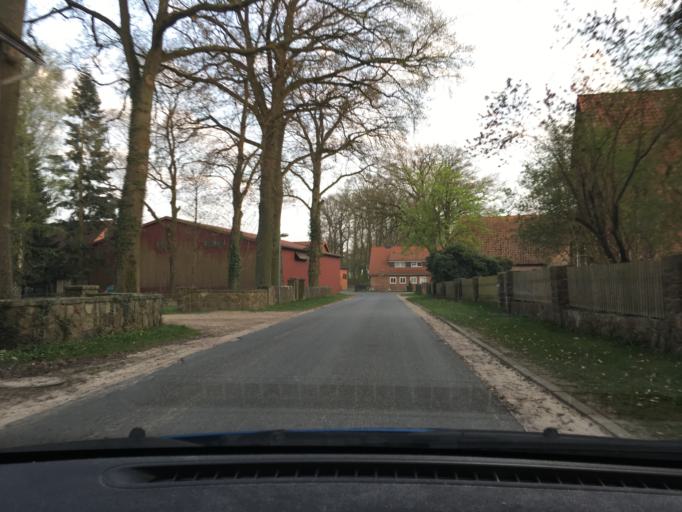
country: DE
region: Lower Saxony
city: Embsen
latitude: 53.1941
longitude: 10.3234
